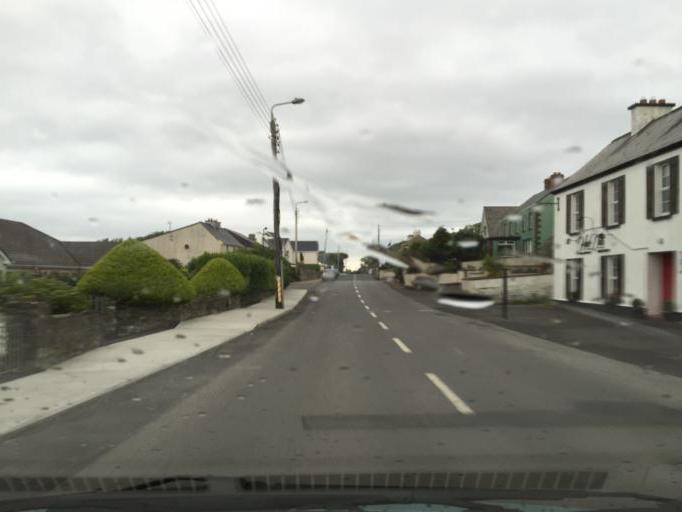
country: IE
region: Connaught
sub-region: Sligo
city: Strandhill
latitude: 54.2654
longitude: -8.5970
